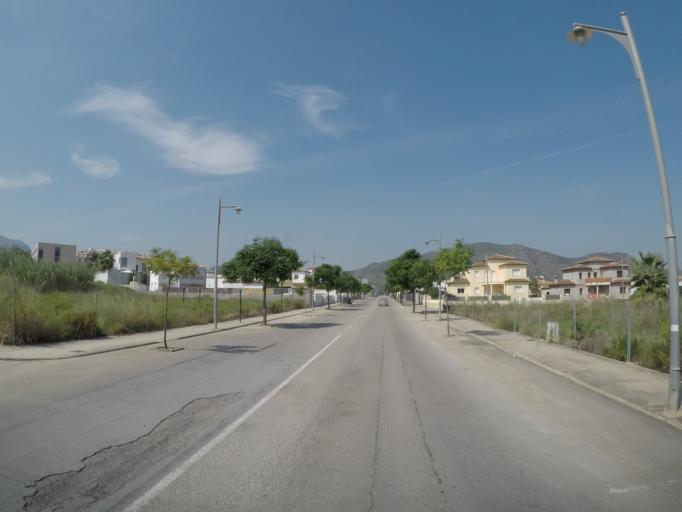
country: ES
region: Valencia
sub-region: Provincia de Alicante
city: Pego
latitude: 38.8452
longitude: -0.1098
